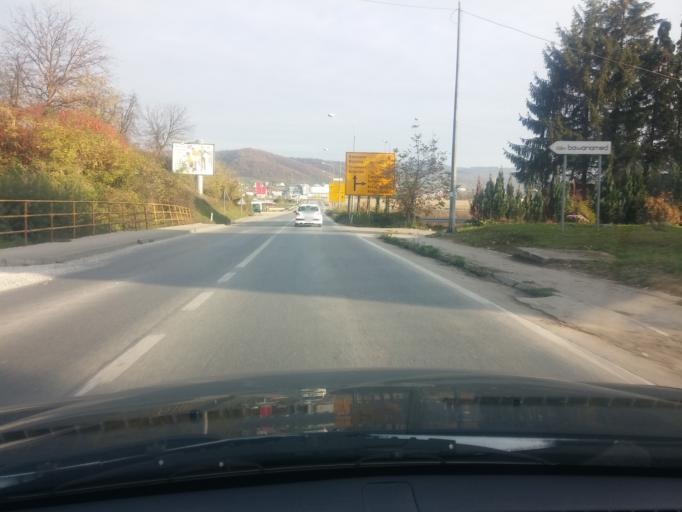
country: BA
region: Republika Srpska
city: Banja Luka
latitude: 44.8205
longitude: 17.1989
